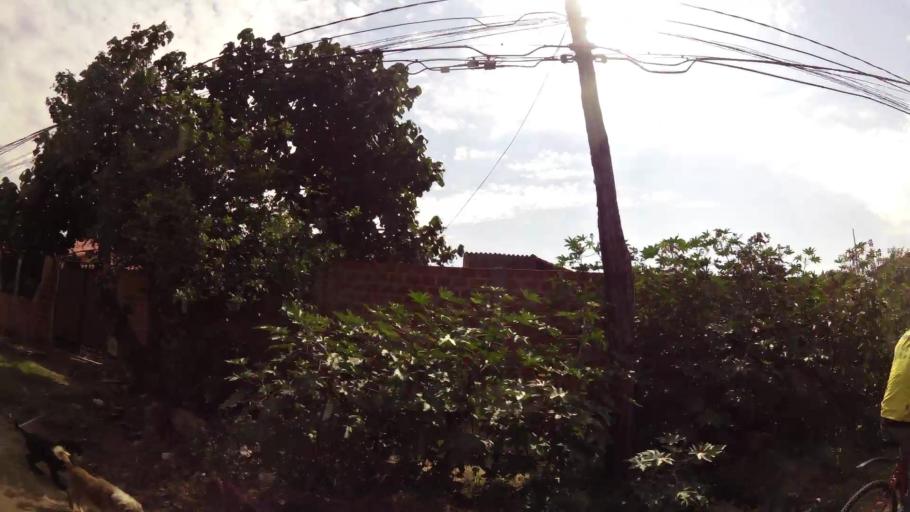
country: BO
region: Santa Cruz
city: Santa Cruz de la Sierra
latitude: -17.7284
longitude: -63.1743
